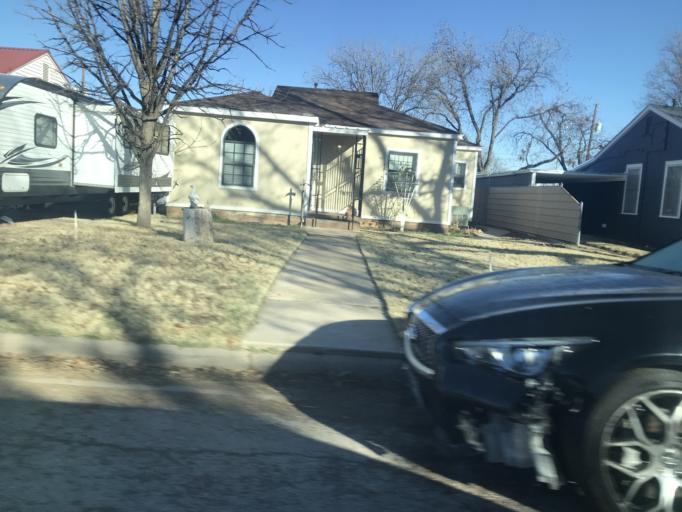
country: US
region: Texas
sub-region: Taylor County
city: Abilene
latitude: 32.4386
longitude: -99.7576
